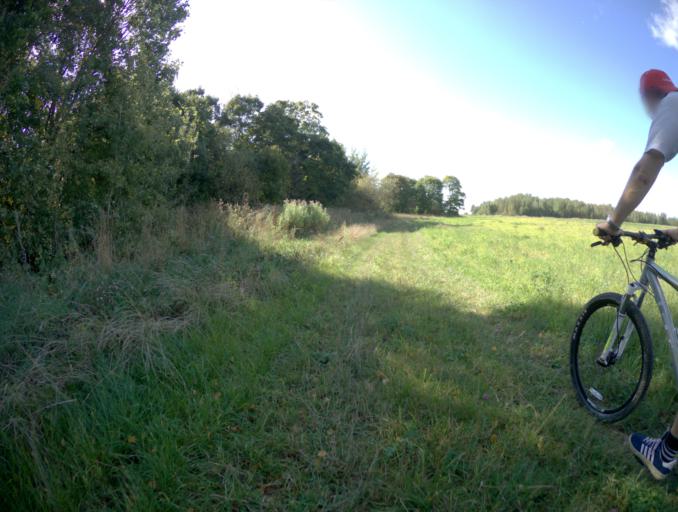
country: RU
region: Vladimir
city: Lakinsk
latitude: 55.8829
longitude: 39.8691
